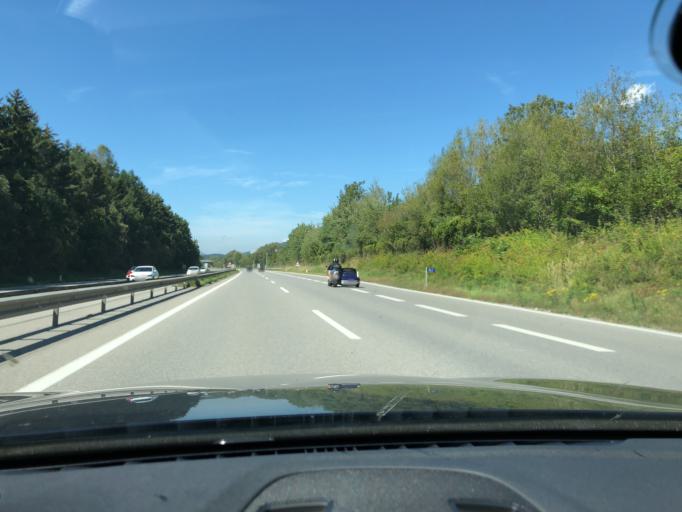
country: AT
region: Vorarlberg
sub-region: Politischer Bezirk Bludenz
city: Nuziders
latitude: 47.1679
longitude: 9.7874
